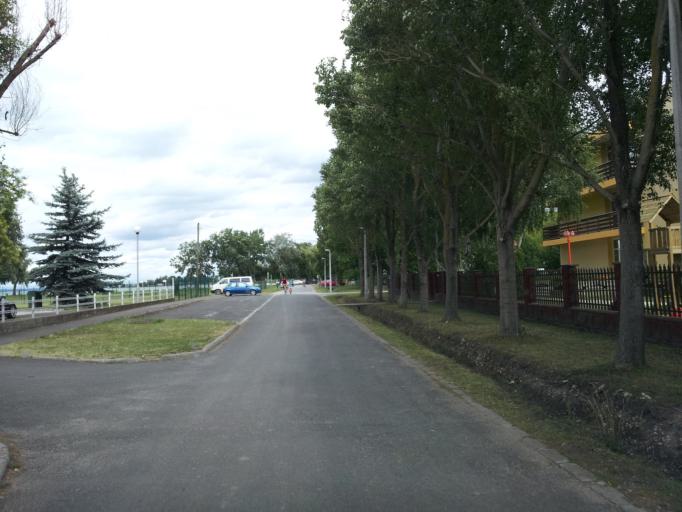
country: HU
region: Somogy
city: Siofok
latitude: 46.9034
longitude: 18.0253
